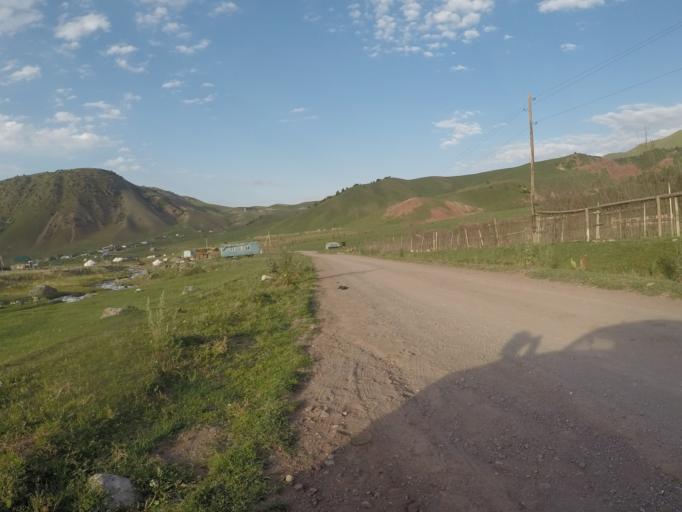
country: KG
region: Chuy
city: Bishkek
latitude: 42.6354
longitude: 74.6165
